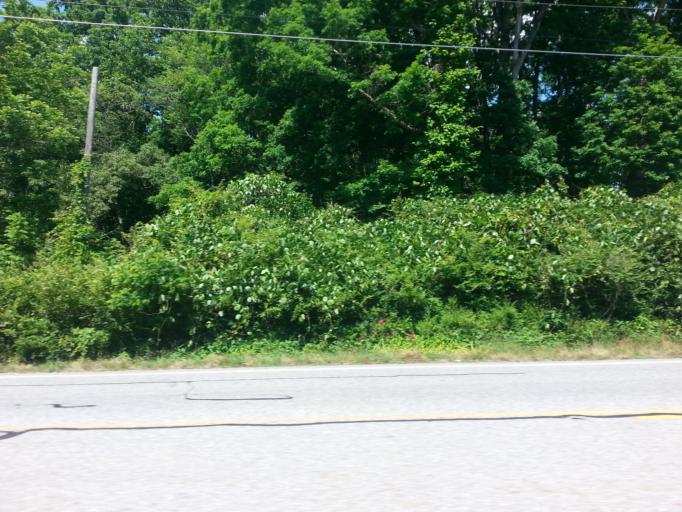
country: US
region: Georgia
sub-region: Union County
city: Blairsville
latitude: 34.9278
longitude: -84.0264
